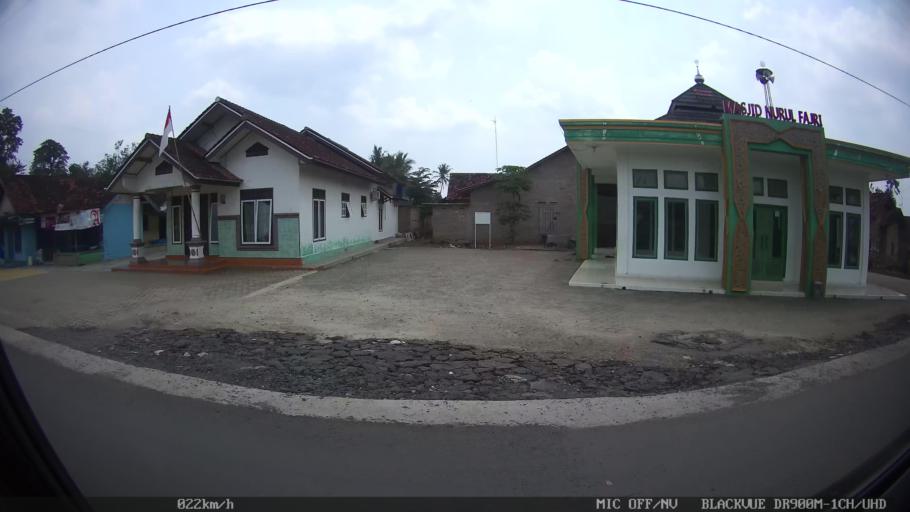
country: ID
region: Lampung
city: Gadingrejo
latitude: -5.3670
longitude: 105.0266
